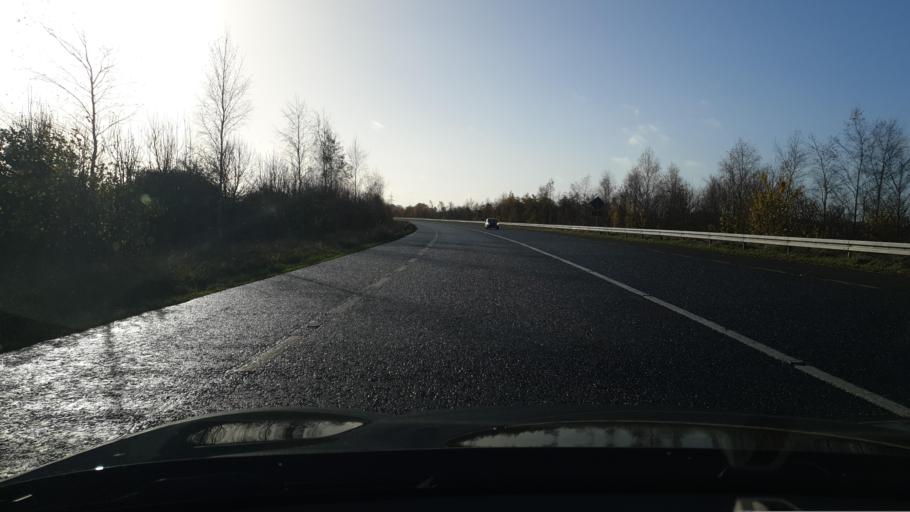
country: IE
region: Leinster
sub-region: An Mhi
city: Dunboyne
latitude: 53.4233
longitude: -6.4891
